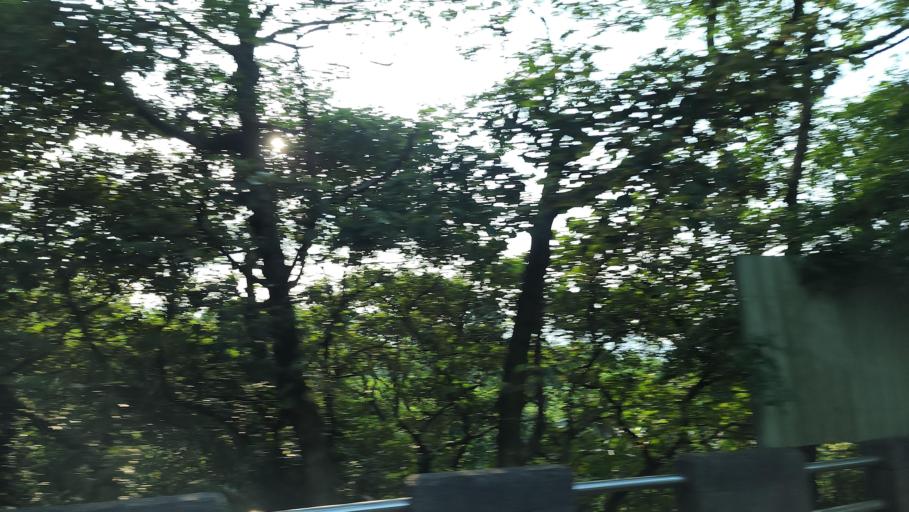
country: TW
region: Taiwan
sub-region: Keelung
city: Keelung
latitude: 25.1784
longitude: 121.6484
